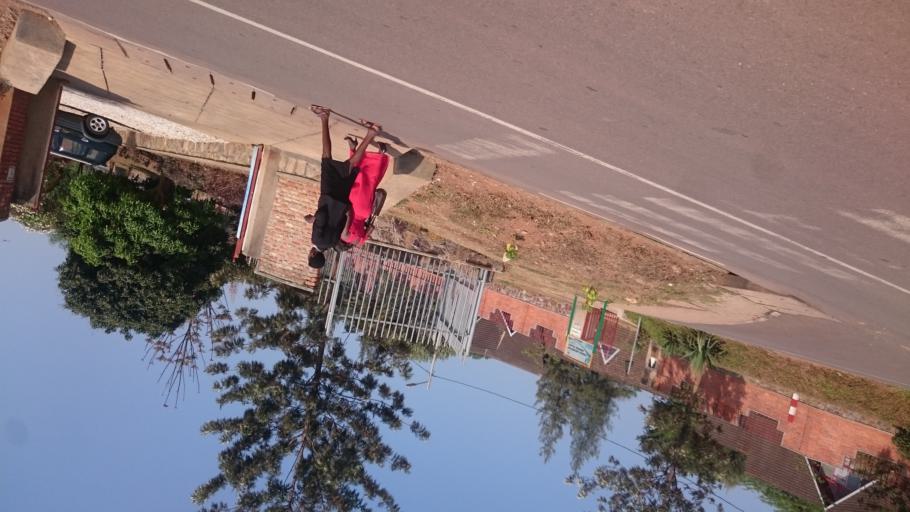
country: RW
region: Kigali
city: Kigali
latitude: -1.9427
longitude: 30.0889
